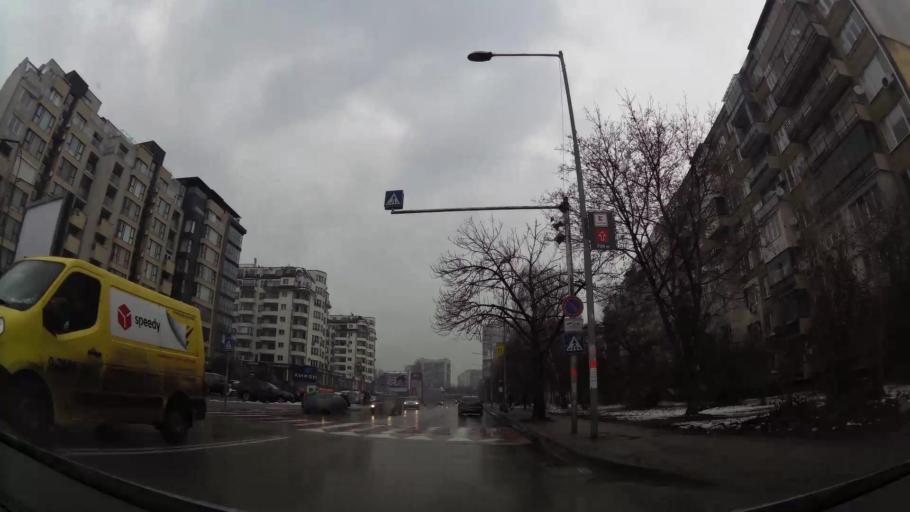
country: BG
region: Sofia-Capital
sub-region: Stolichna Obshtina
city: Sofia
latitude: 42.6670
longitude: 23.2831
